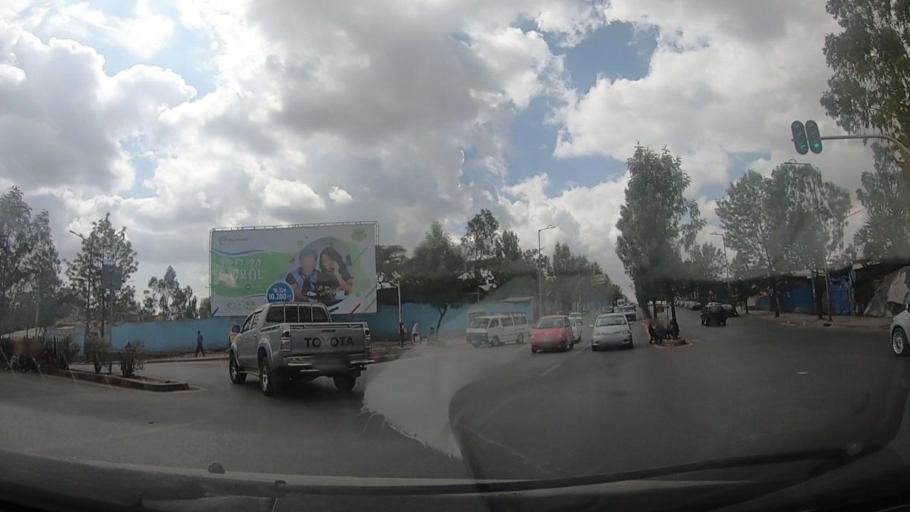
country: ET
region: Adis Abeba
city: Addis Ababa
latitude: 9.0038
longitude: 38.7337
